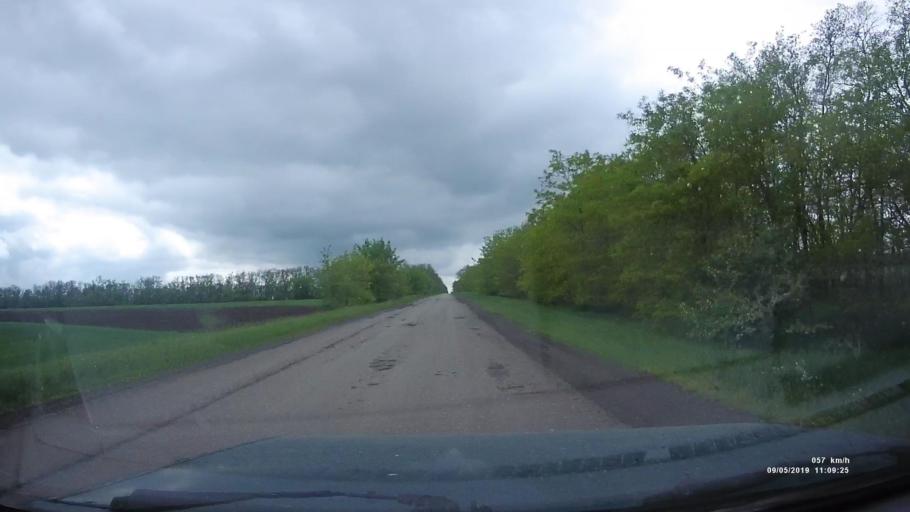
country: RU
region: Krasnodarskiy
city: Kanelovskaya
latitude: 46.7833
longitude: 39.2117
